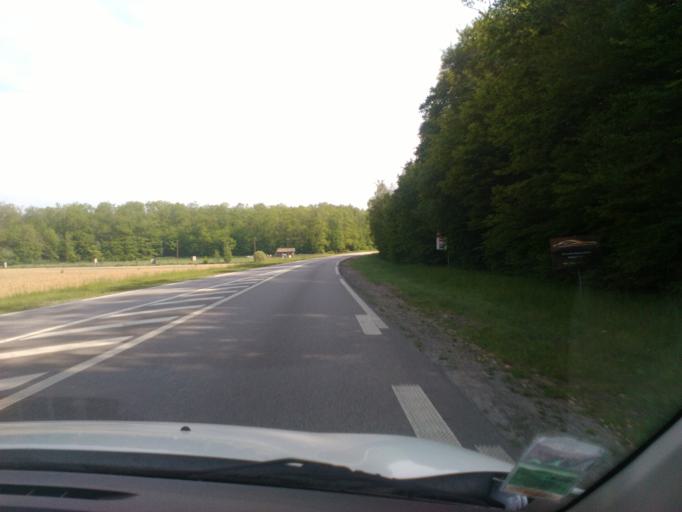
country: FR
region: Lorraine
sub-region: Departement des Vosges
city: Golbey
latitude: 48.2100
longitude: 6.4194
